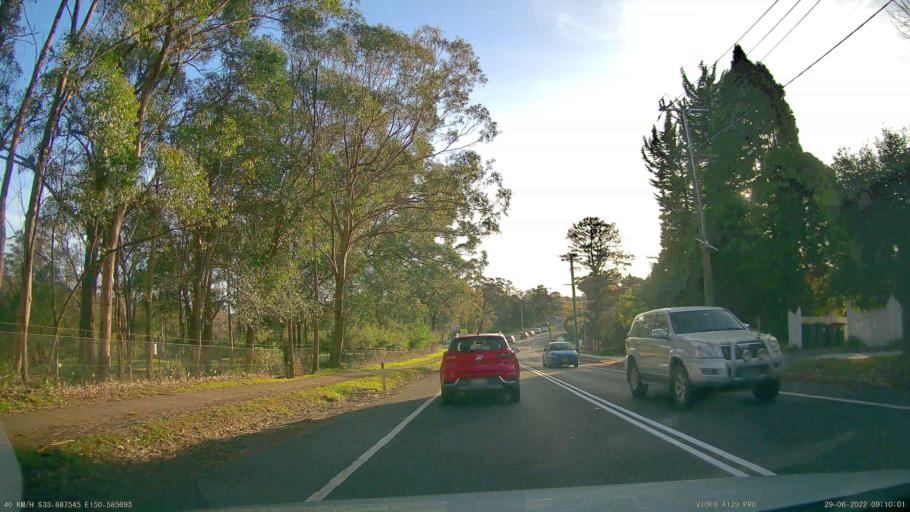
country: AU
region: New South Wales
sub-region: Blue Mountains Municipality
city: Blaxland
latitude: -33.6873
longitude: 150.5858
